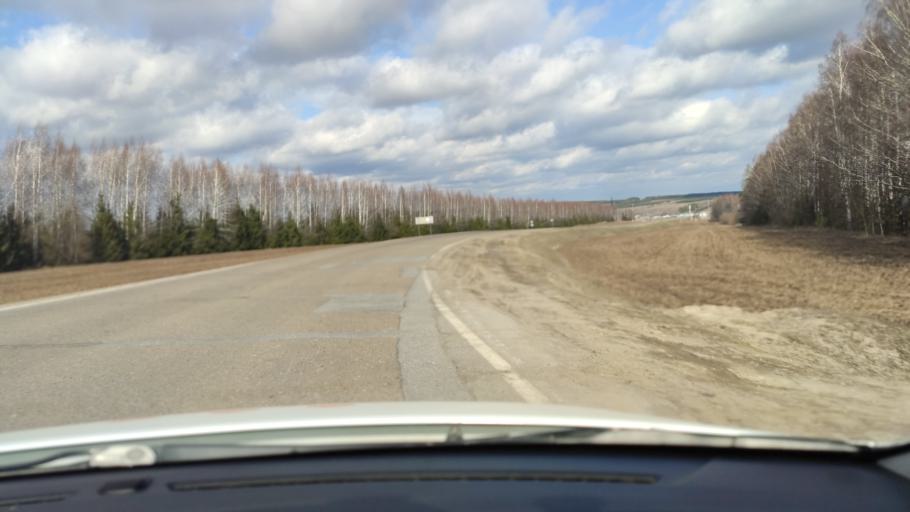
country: RU
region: Tatarstan
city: Vysokaya Gora
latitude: 56.1121
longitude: 49.1851
